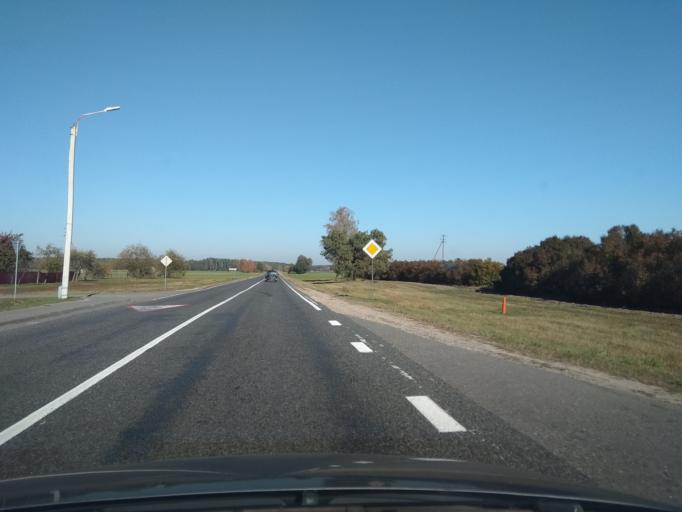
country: BY
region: Brest
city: Kobryn
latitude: 52.1192
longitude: 24.3054
